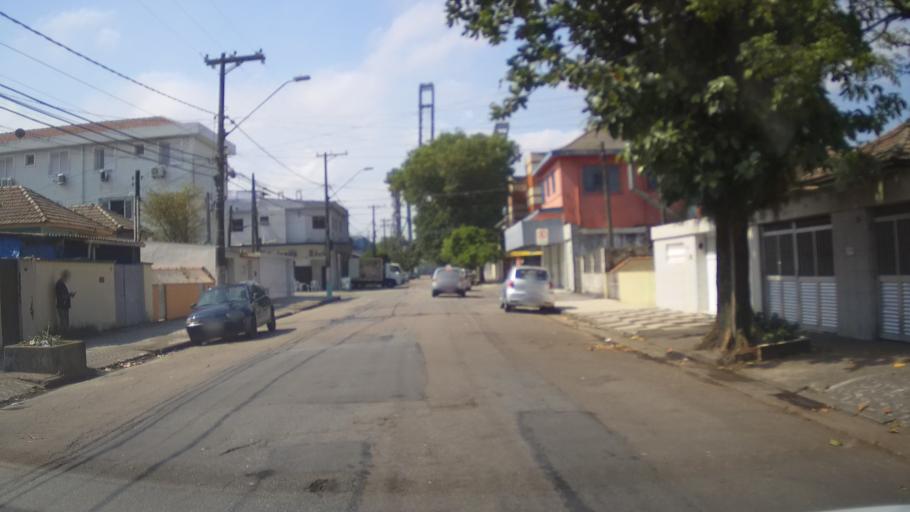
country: BR
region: Sao Paulo
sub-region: Santos
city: Santos
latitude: -23.9770
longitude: -46.2962
